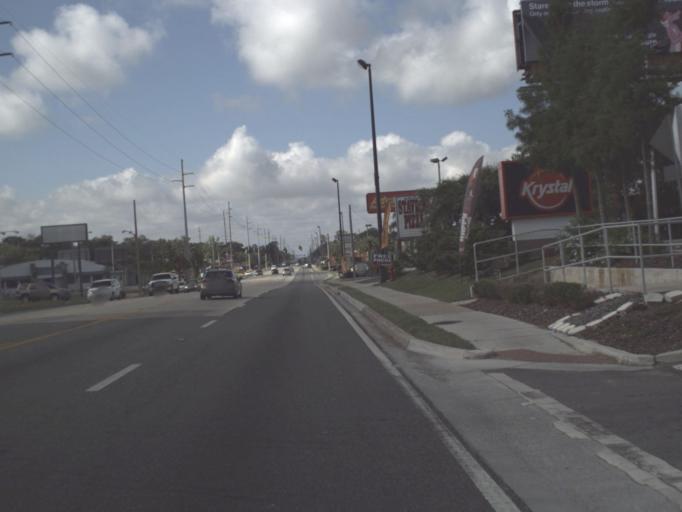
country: US
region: Florida
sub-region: Lake County
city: Leesburg
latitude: 28.8213
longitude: -81.8875
